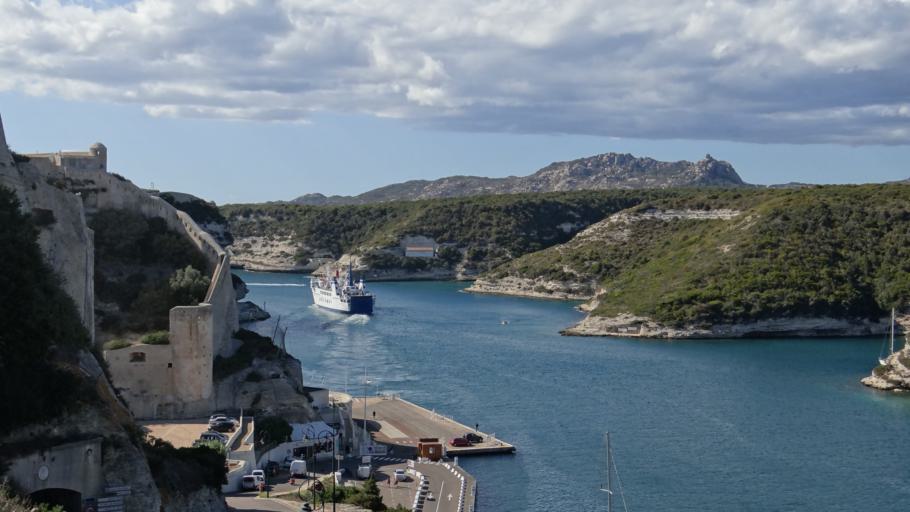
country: FR
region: Corsica
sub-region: Departement de la Corse-du-Sud
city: Bonifacio
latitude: 41.3882
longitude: 9.1593
